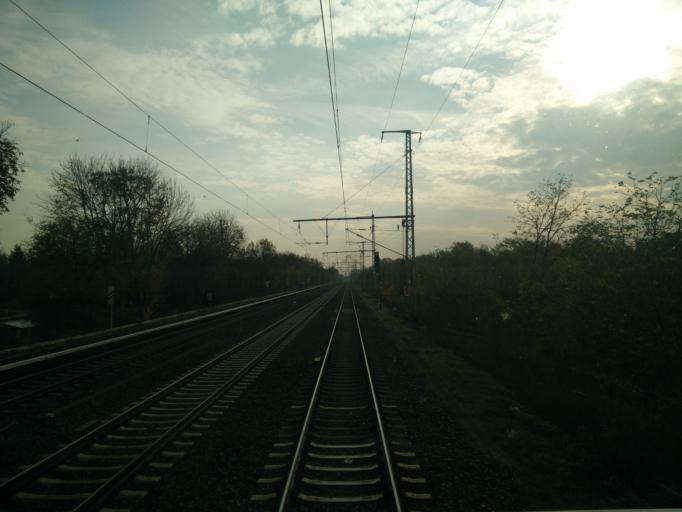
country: DE
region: Berlin
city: Karlshorst
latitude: 52.4748
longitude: 13.5397
